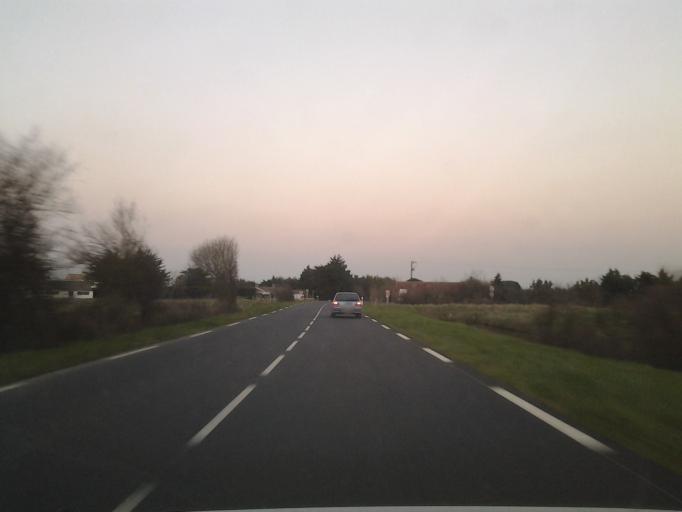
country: FR
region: Pays de la Loire
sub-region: Departement de la Vendee
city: Beauvoir-sur-Mer
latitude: 46.9152
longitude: -2.0626
